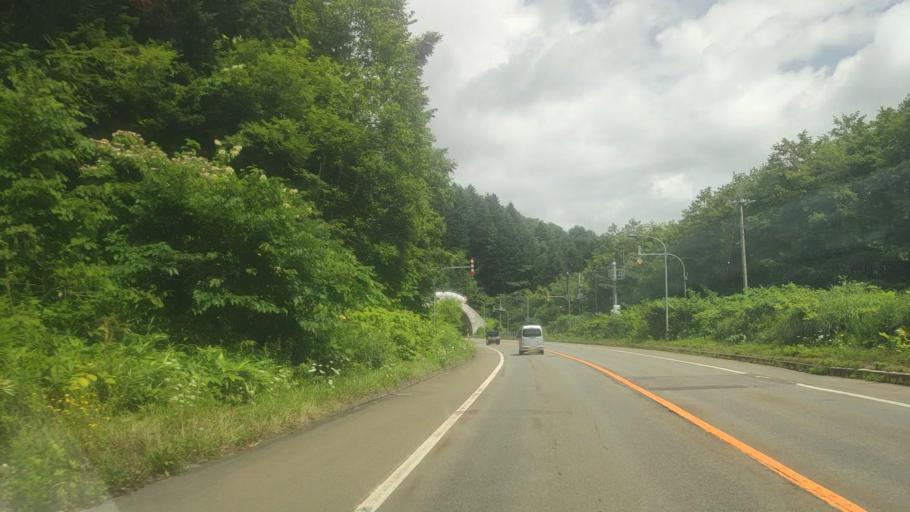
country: JP
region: Hokkaido
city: Niseko Town
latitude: 42.6010
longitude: 140.5569
